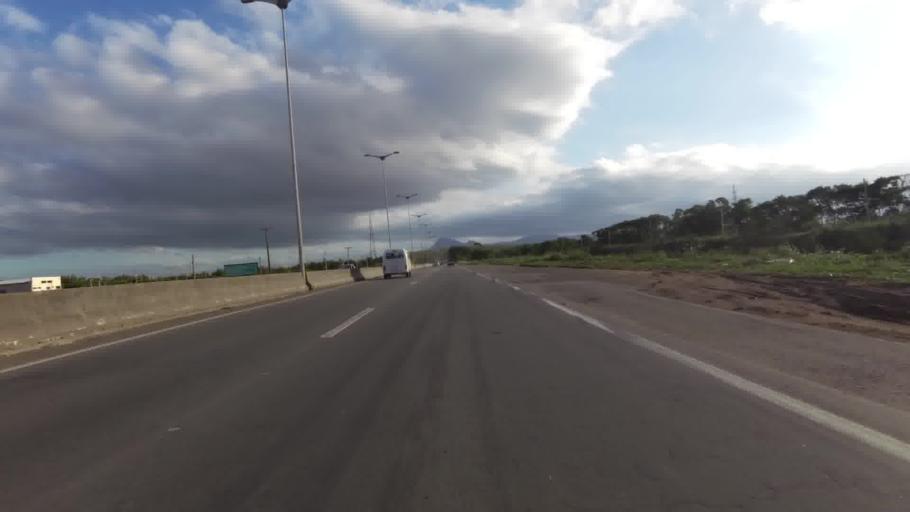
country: BR
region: Espirito Santo
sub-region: Serra
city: Serra
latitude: -20.2113
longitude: -40.3188
